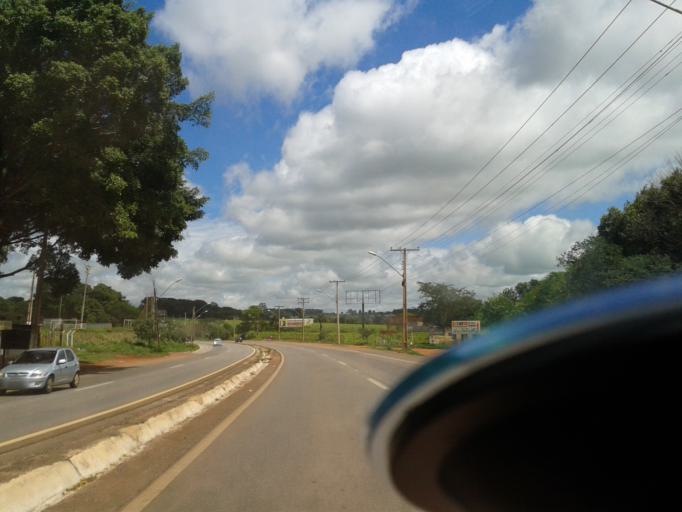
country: BR
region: Goias
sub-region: Goianira
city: Goianira
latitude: -16.4967
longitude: -49.4213
